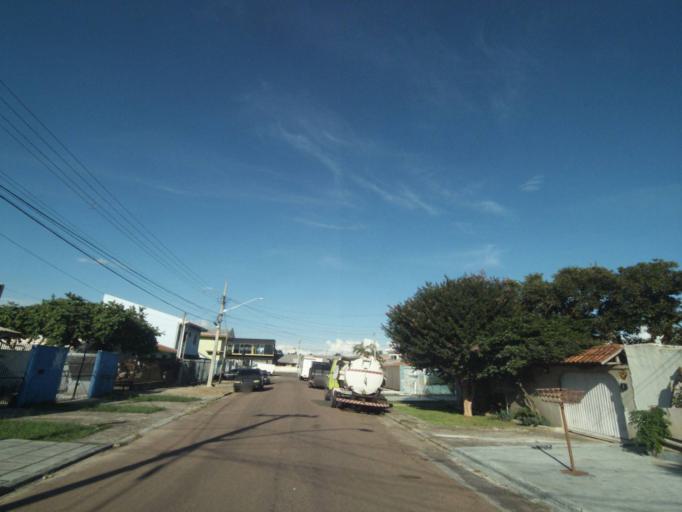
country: BR
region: Parana
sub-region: Pinhais
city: Pinhais
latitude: -25.4537
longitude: -49.2039
